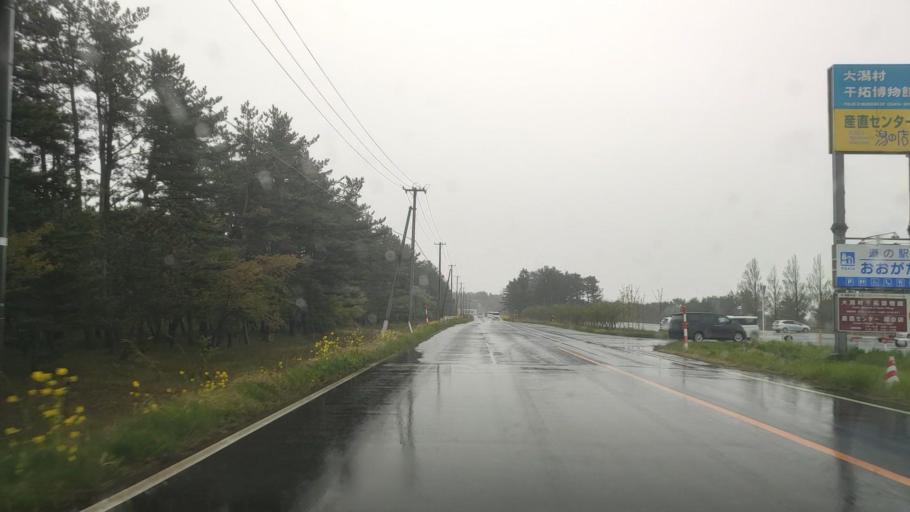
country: JP
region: Akita
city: Tenno
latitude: 40.0160
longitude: 139.9528
